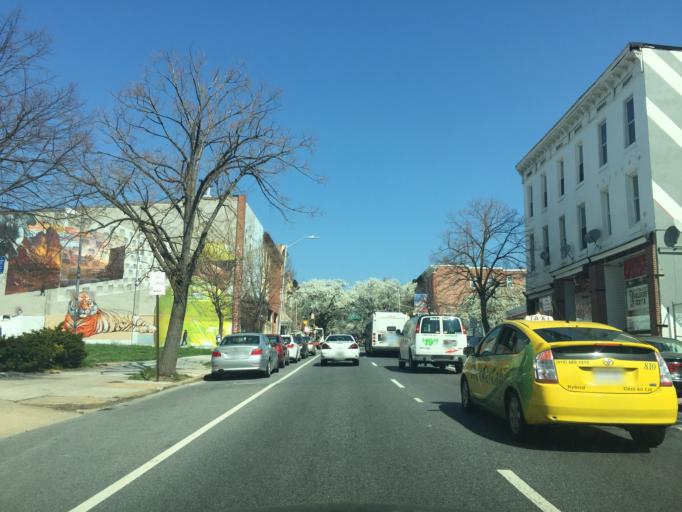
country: US
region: Maryland
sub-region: City of Baltimore
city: Baltimore
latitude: 39.3123
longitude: -76.6166
